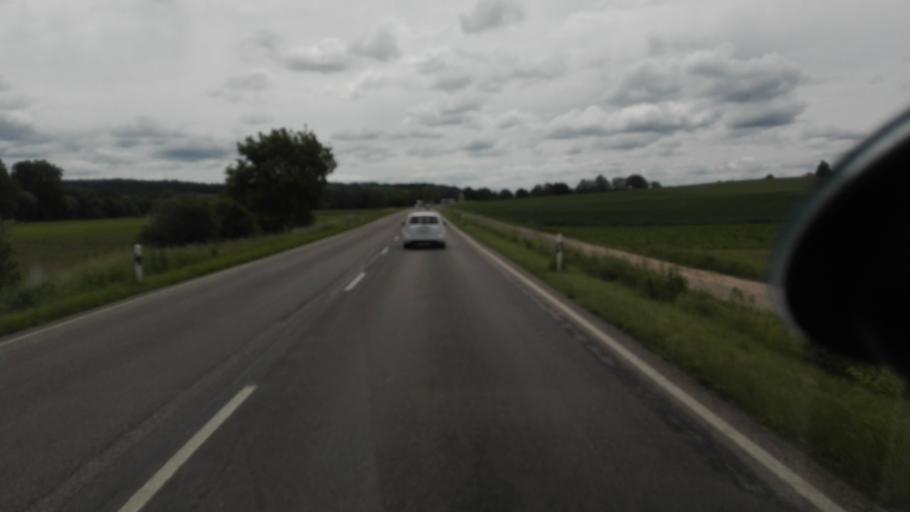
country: DE
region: Baden-Wuerttemberg
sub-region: Karlsruhe Region
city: Gondelsheim
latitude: 49.0779
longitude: 8.6529
